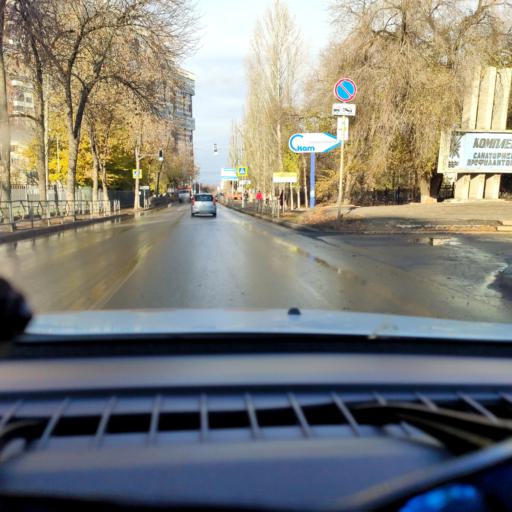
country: RU
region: Samara
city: Samara
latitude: 53.2355
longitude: 50.1845
